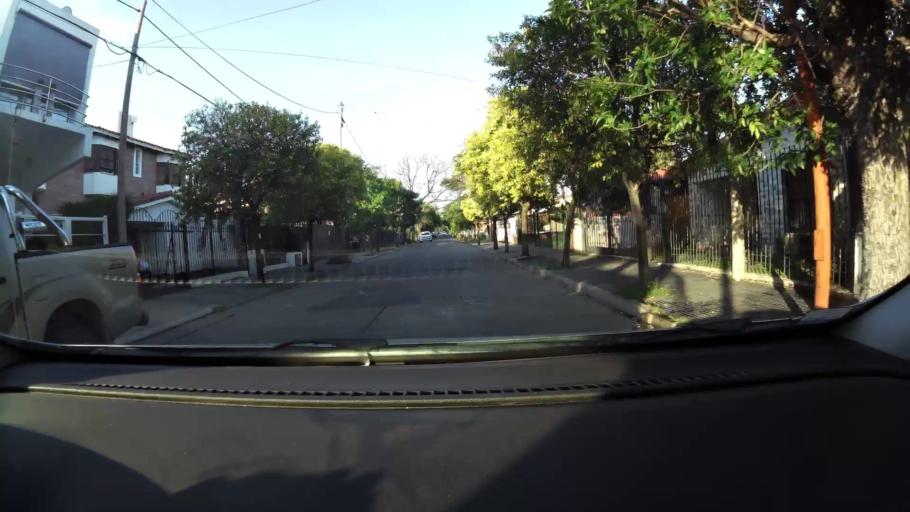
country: AR
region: Cordoba
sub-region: Departamento de Capital
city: Cordoba
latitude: -31.3782
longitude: -64.2338
